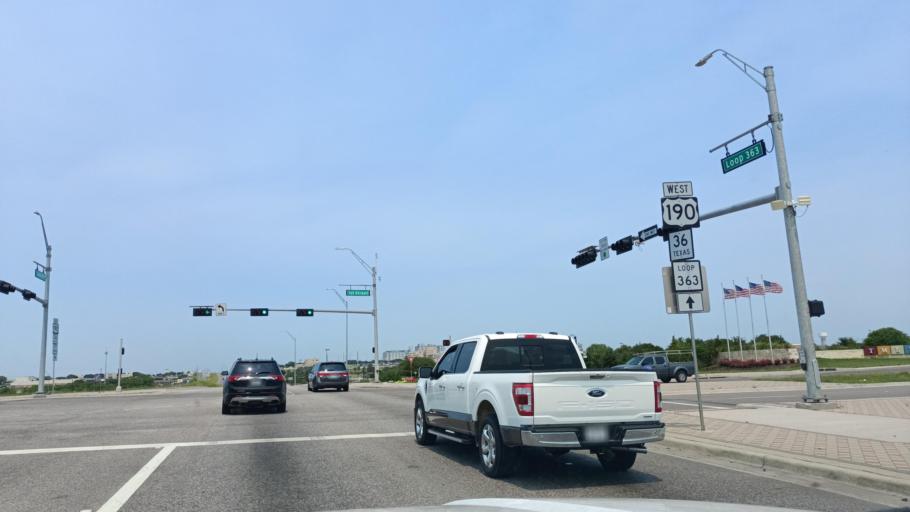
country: US
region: Texas
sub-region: Bell County
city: Temple
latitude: 31.0685
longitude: -97.3490
